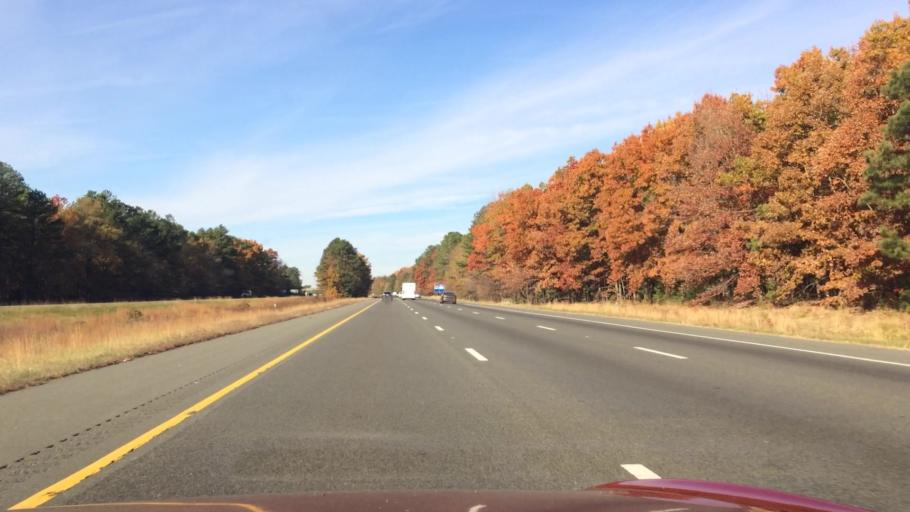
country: US
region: Virginia
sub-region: Henrico County
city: Glen Allen
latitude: 37.6791
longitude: -77.5108
